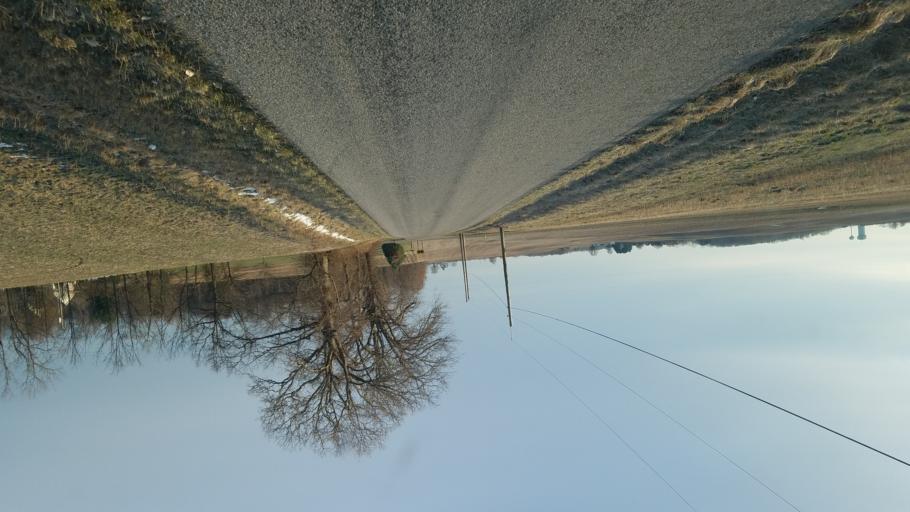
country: US
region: Ohio
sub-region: Knox County
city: Centerburg
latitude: 40.4105
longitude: -82.7209
